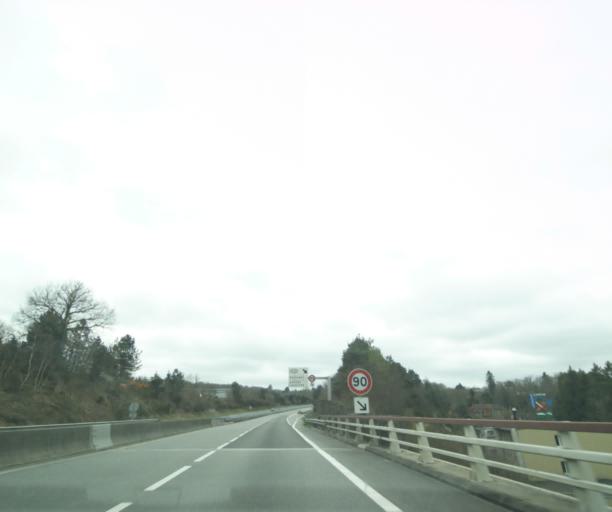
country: FR
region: Limousin
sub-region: Departement de la Haute-Vienne
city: Bessines-sur-Gartempe
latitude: 46.1143
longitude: 1.3754
